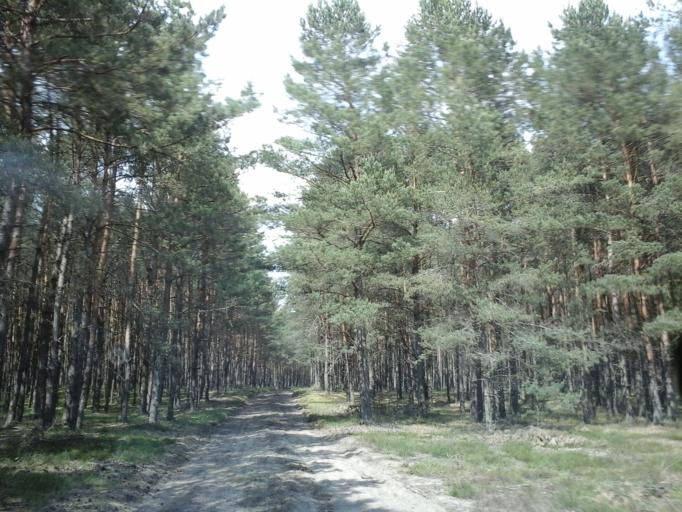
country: PL
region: West Pomeranian Voivodeship
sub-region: Powiat choszczenski
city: Drawno
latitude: 53.1355
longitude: 15.7658
